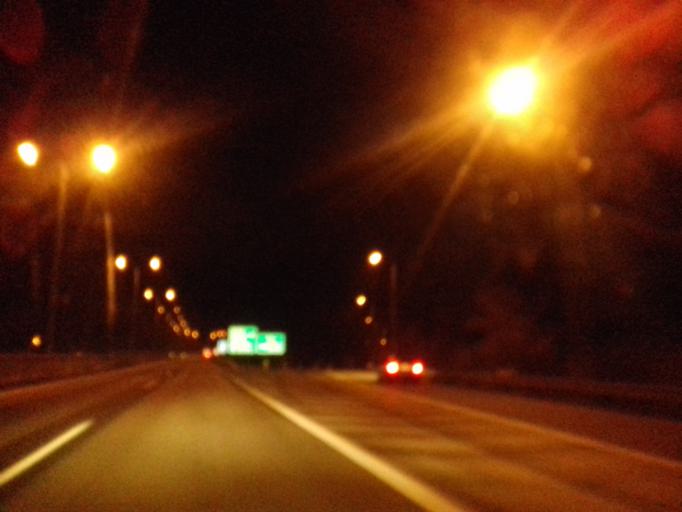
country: CZ
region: South Moravian
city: Ostopovice
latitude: 49.1683
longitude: 16.5476
